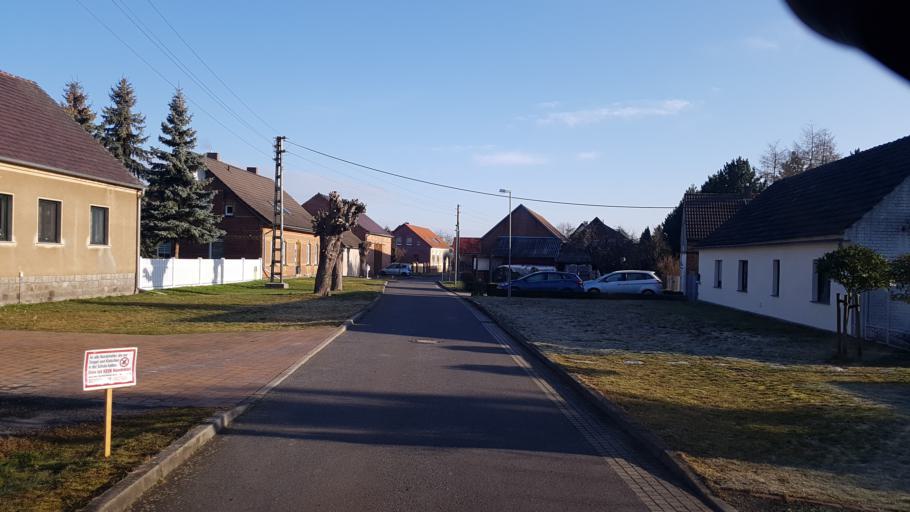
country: DE
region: Brandenburg
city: Lubbenau
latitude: 51.8163
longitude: 13.9028
